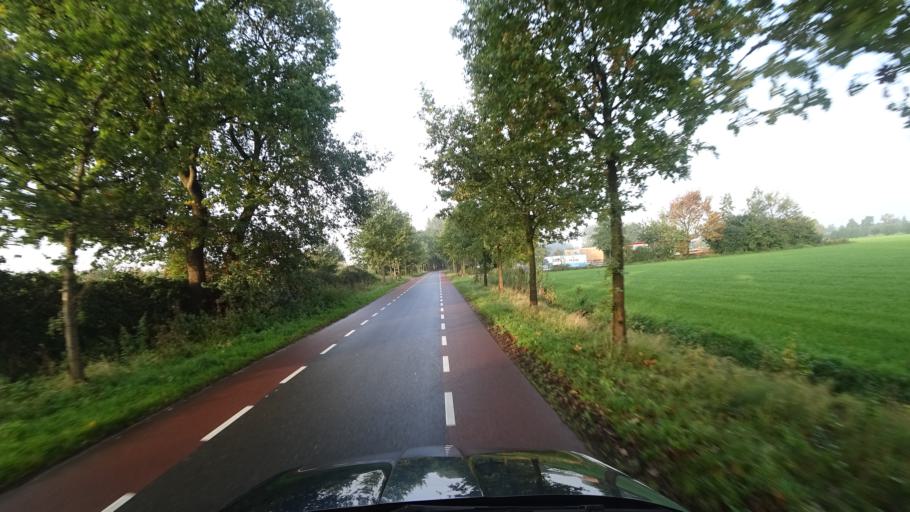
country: NL
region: Gelderland
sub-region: Gemeente Ede
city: Ede
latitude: 52.0058
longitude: 5.6324
